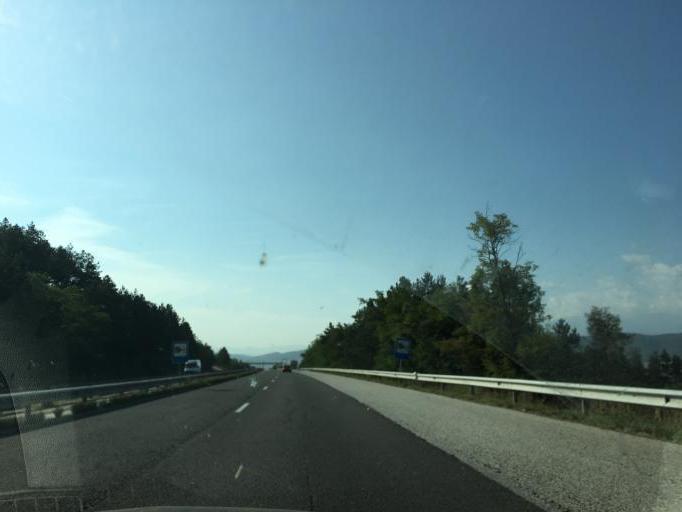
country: BG
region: Sofiya
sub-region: Obshtina Ikhtiman
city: Ikhtiman
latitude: 42.4370
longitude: 23.8500
